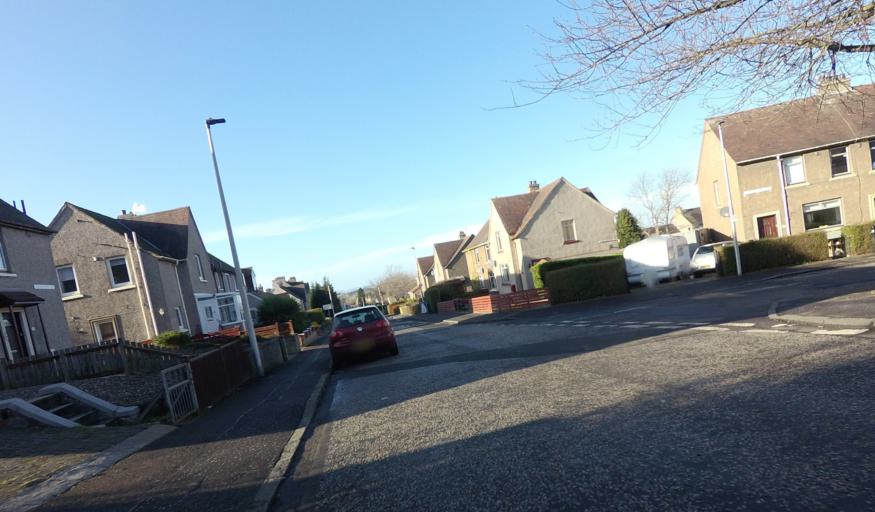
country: GB
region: Scotland
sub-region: Edinburgh
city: Colinton
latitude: 55.9592
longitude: -3.2870
